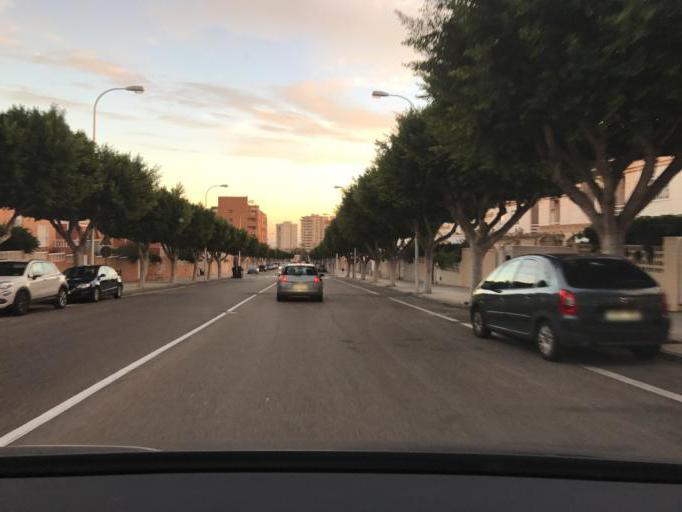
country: ES
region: Andalusia
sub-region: Provincia de Almeria
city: Aguadulce
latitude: 36.8157
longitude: -2.5801
